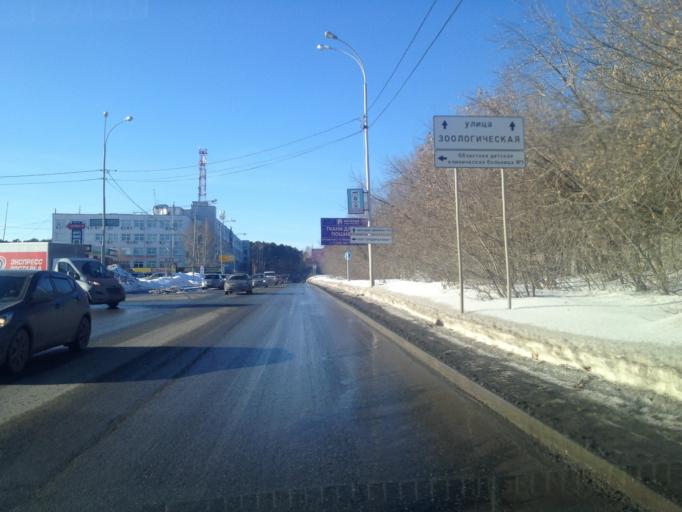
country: RU
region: Sverdlovsk
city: Sovkhoznyy
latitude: 56.8126
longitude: 60.5399
